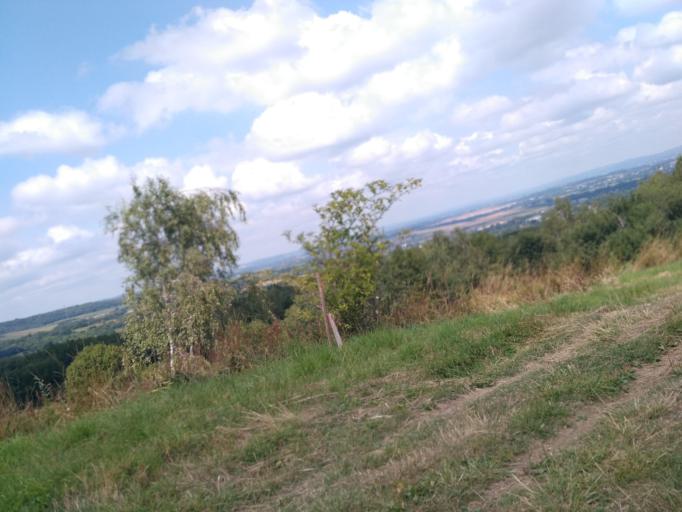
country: PL
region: Subcarpathian Voivodeship
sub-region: Powiat krosnienski
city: Iwonicz-Zdroj
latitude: 49.5834
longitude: 21.8071
